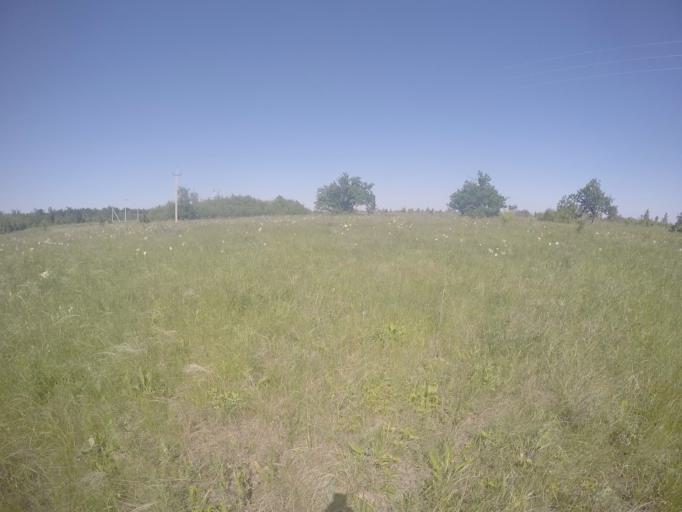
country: RU
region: Saratov
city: Krasnyy Oktyabr'
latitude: 51.3084
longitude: 45.5832
